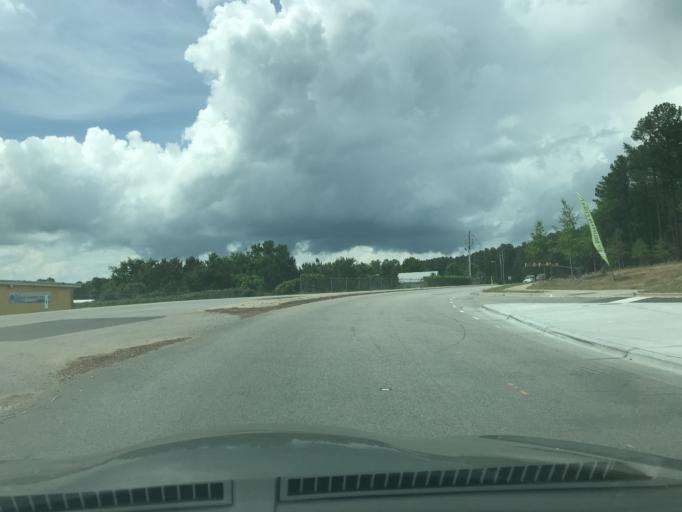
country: US
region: North Carolina
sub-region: Wake County
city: Wake Forest
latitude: 35.8807
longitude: -78.5741
